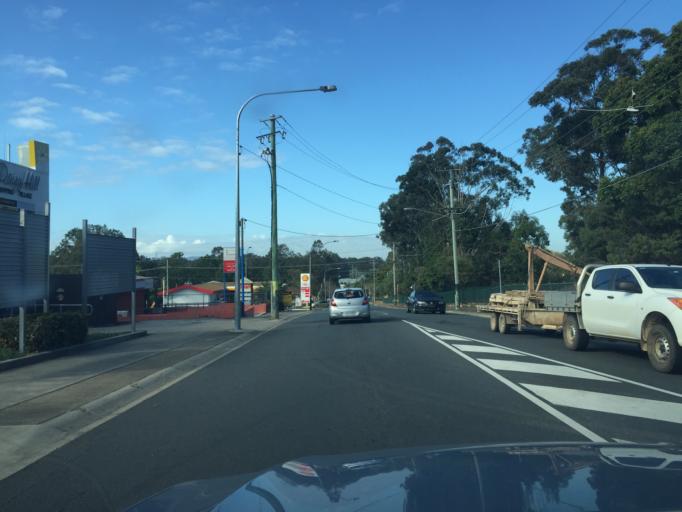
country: AU
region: Queensland
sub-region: Logan
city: Slacks Creek
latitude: -27.6434
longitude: 153.1535
